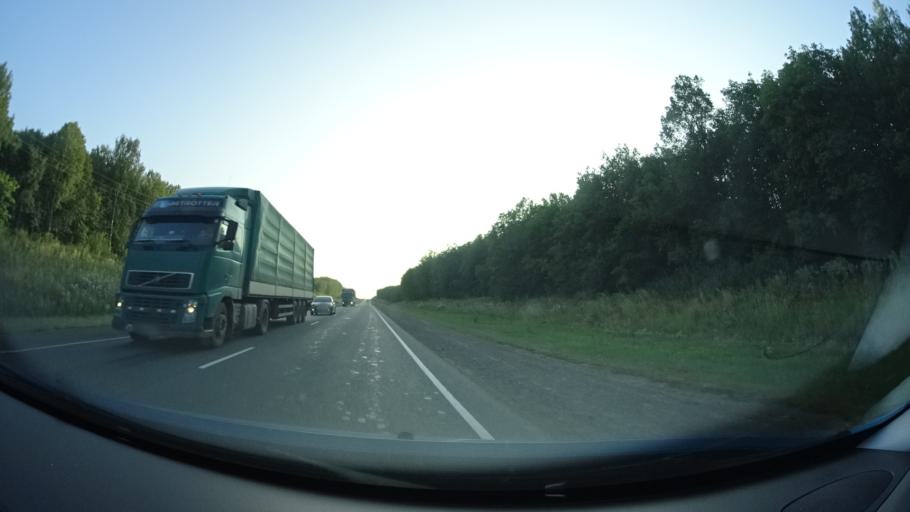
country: RU
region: Samara
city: Isakly
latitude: 54.0106
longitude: 51.6779
